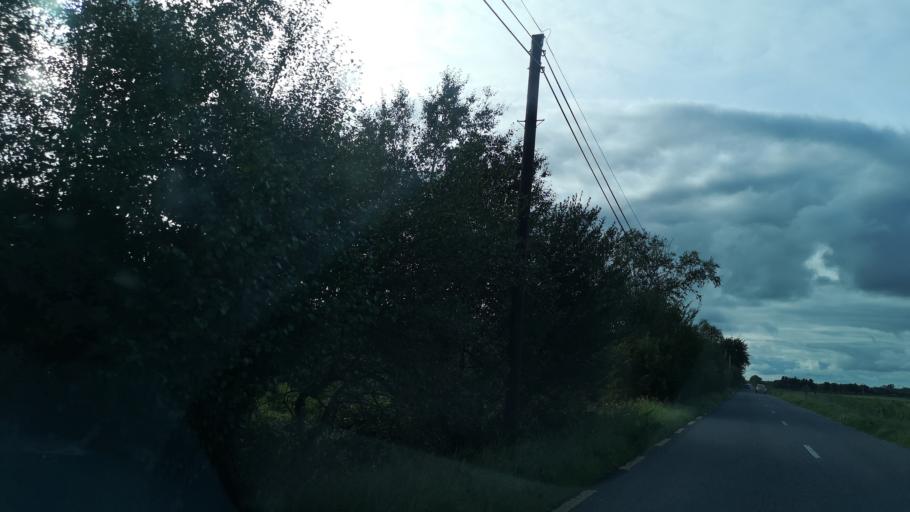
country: IE
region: Leinster
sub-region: Uibh Fhaili
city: Banagher
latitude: 53.2819
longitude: -8.0690
